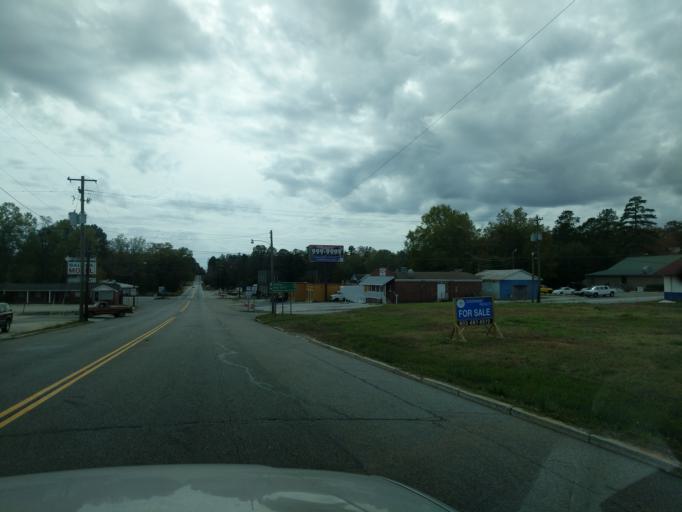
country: US
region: South Carolina
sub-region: Saluda County
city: Saluda
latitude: 34.0005
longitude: -81.7720
